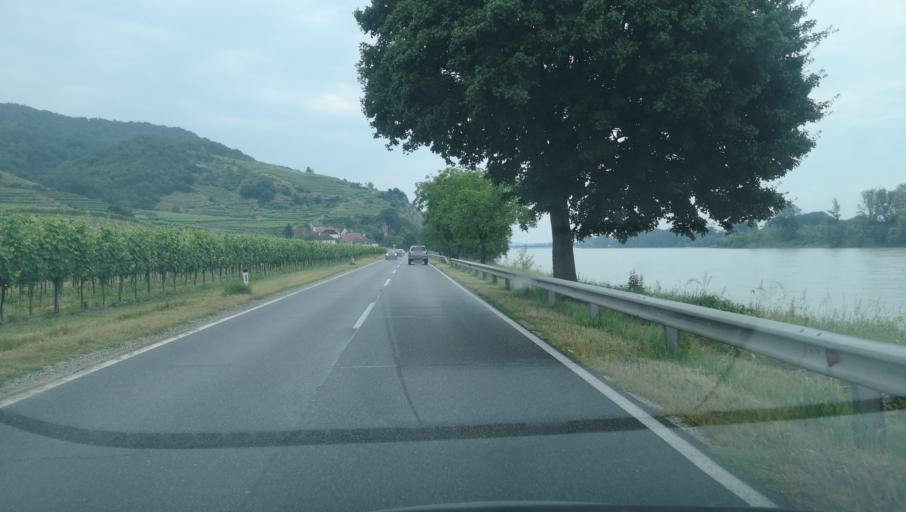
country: AT
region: Lower Austria
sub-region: Politischer Bezirk Krems
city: Durnstein
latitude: 48.3905
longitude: 15.5520
